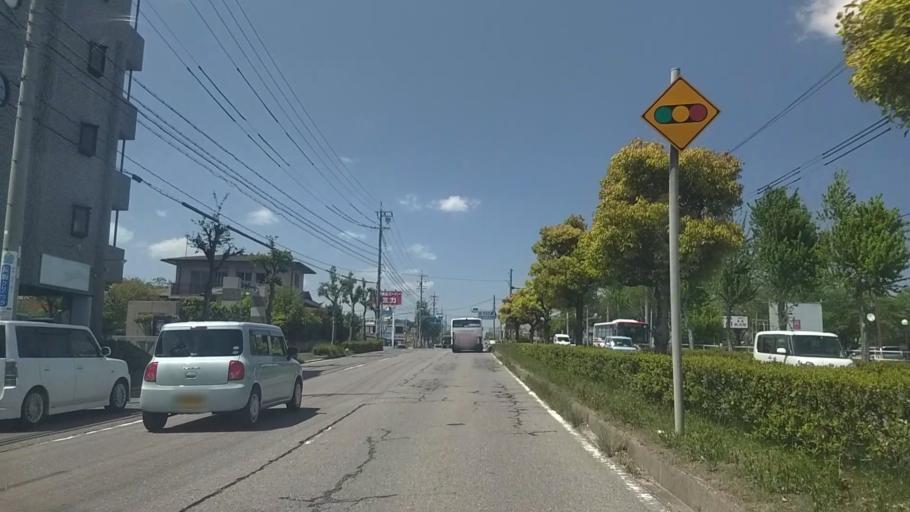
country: JP
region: Aichi
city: Okazaki
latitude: 34.9666
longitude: 137.1827
